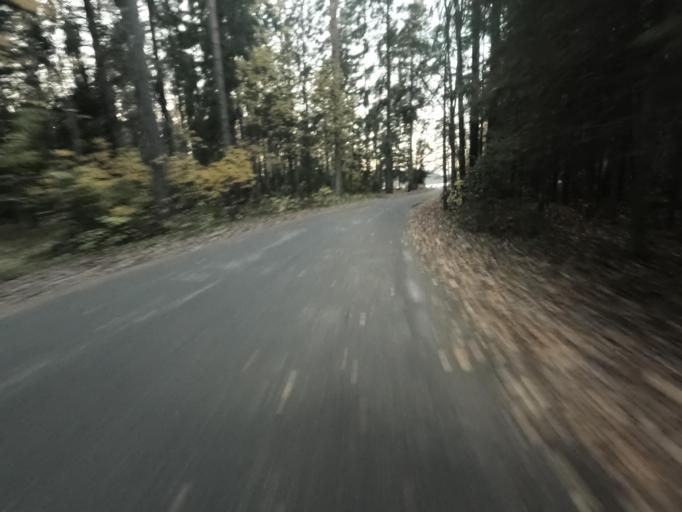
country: RU
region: St.-Petersburg
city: Komarovo
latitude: 60.2075
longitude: 29.7894
